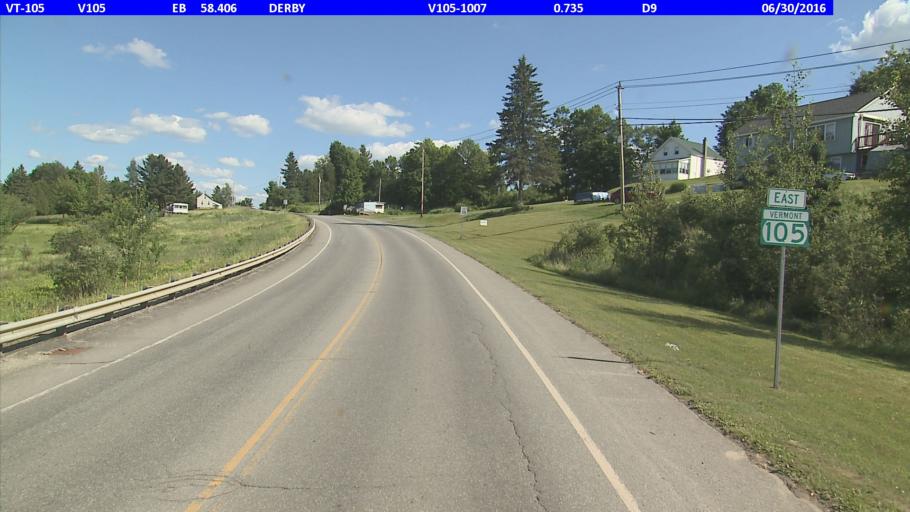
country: US
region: Vermont
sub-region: Orleans County
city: Newport
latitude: 44.9443
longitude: -72.1344
